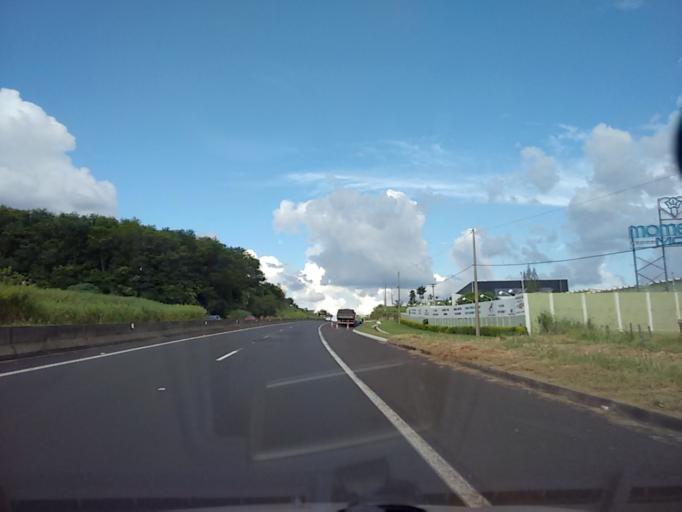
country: BR
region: Sao Paulo
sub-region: Marilia
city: Marilia
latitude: -22.2152
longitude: -49.8457
